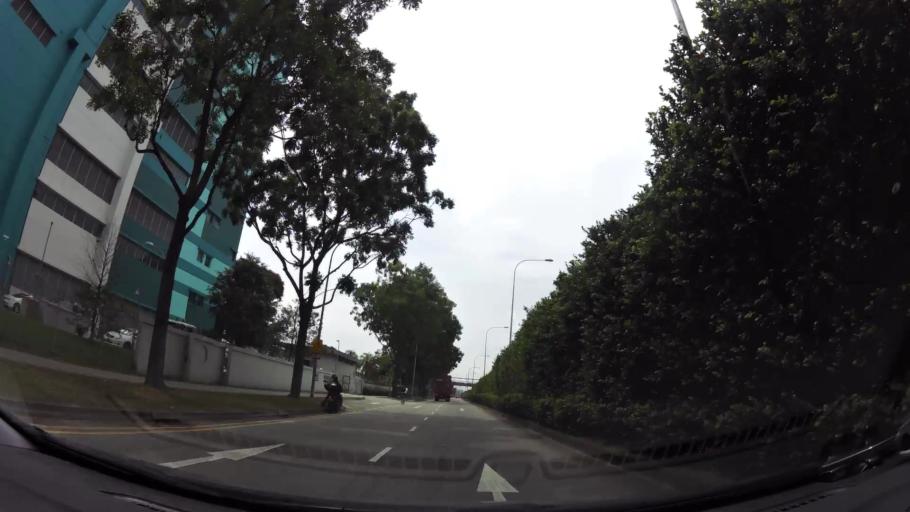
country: MY
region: Johor
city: Johor Bahru
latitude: 1.3223
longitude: 103.6949
